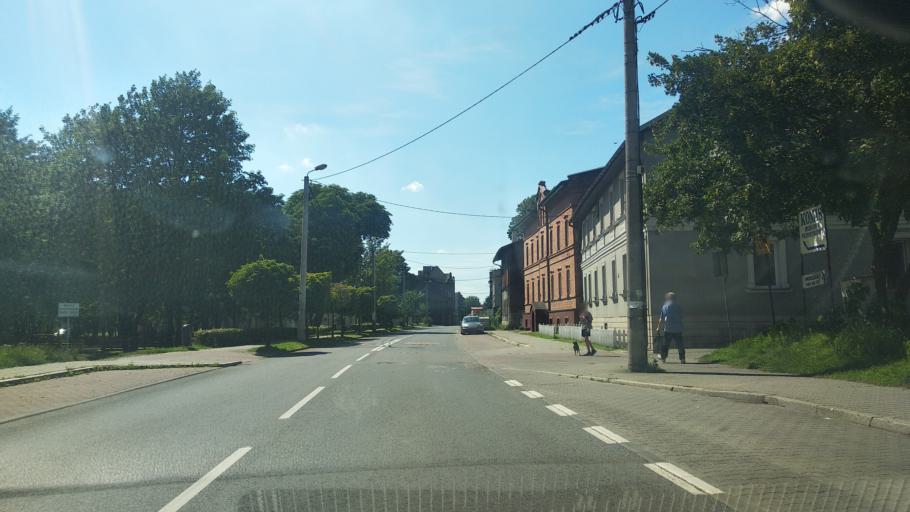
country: PL
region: Silesian Voivodeship
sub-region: Sosnowiec
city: Sosnowiec
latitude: 50.2655
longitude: 19.0947
